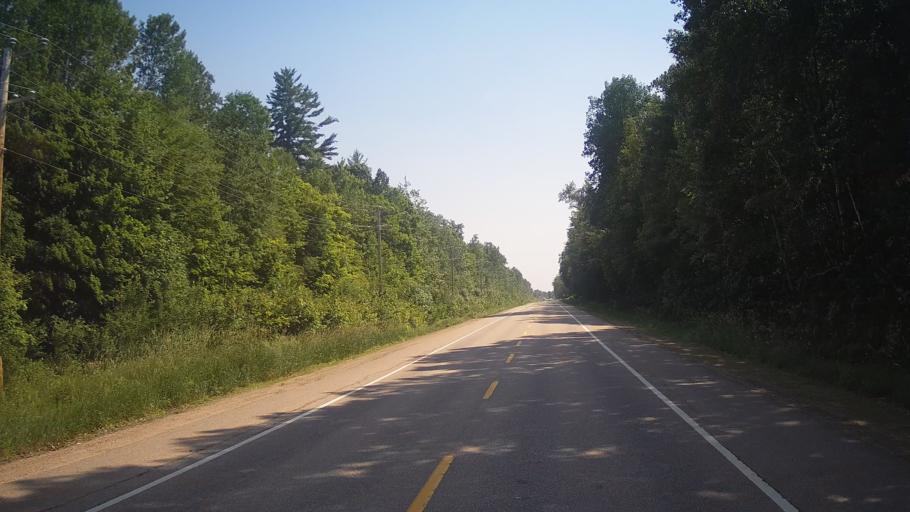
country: CA
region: Ontario
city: Pembroke
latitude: 45.8418
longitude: -77.0134
